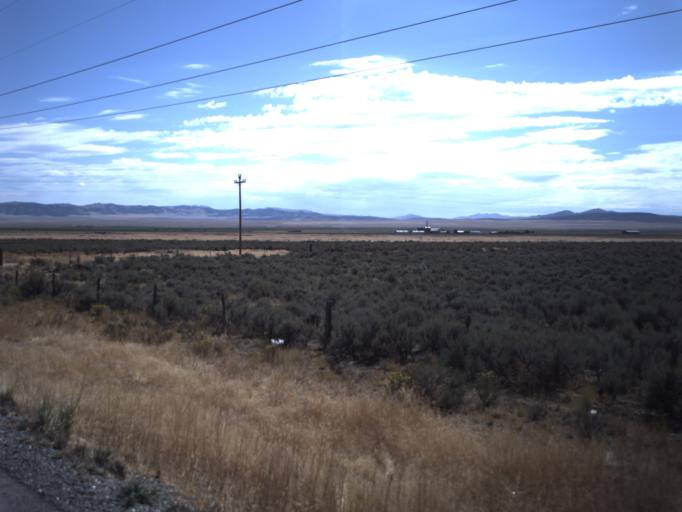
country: US
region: Idaho
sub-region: Oneida County
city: Malad City
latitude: 41.9659
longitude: -112.9817
